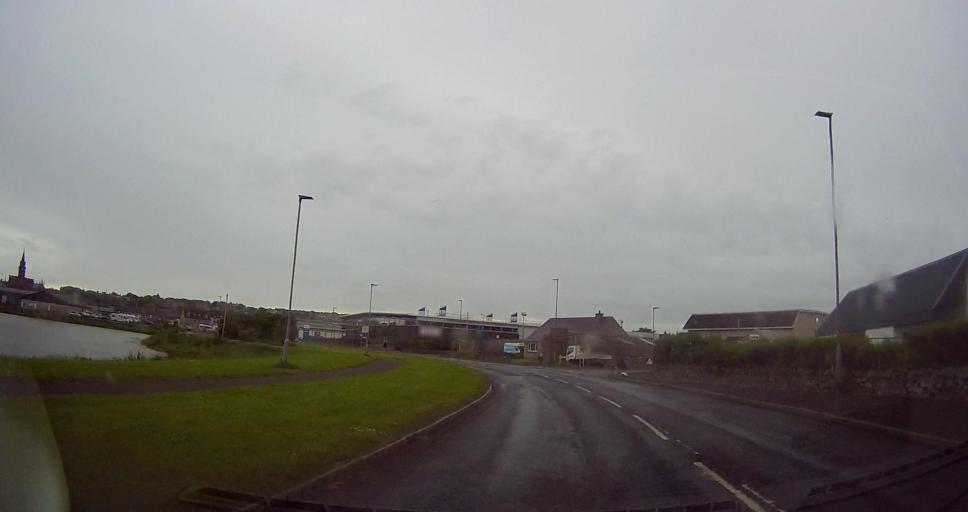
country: GB
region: Scotland
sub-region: Orkney Islands
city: Orkney
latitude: 58.9820
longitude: -2.9697
